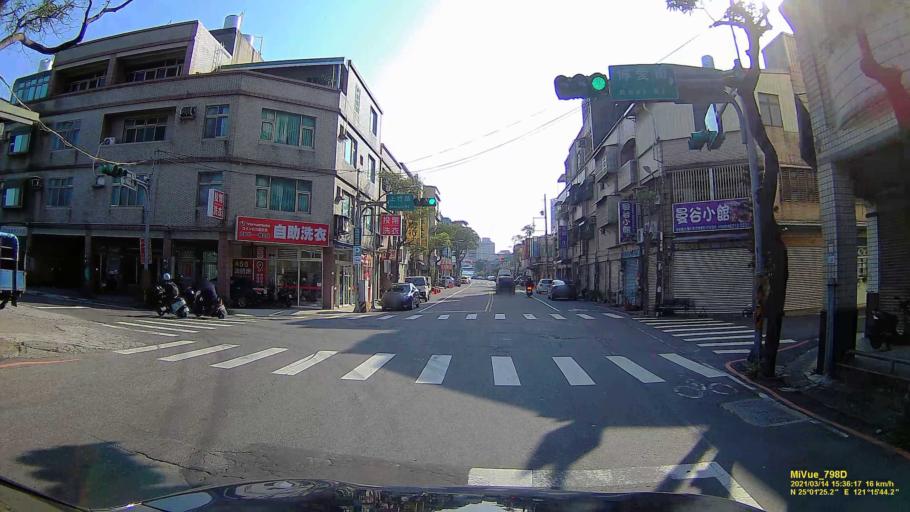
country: TW
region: Taiwan
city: Taoyuan City
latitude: 25.0236
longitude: 121.2622
